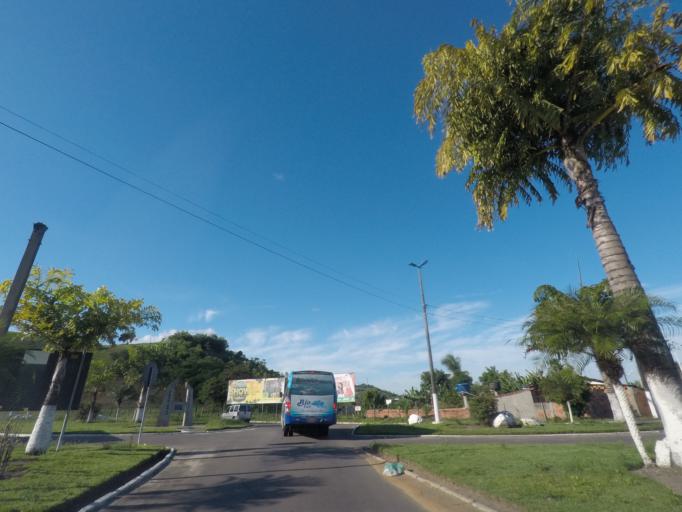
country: BR
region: Bahia
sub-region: Nazare
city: Nazare
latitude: -13.0429
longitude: -39.0051
